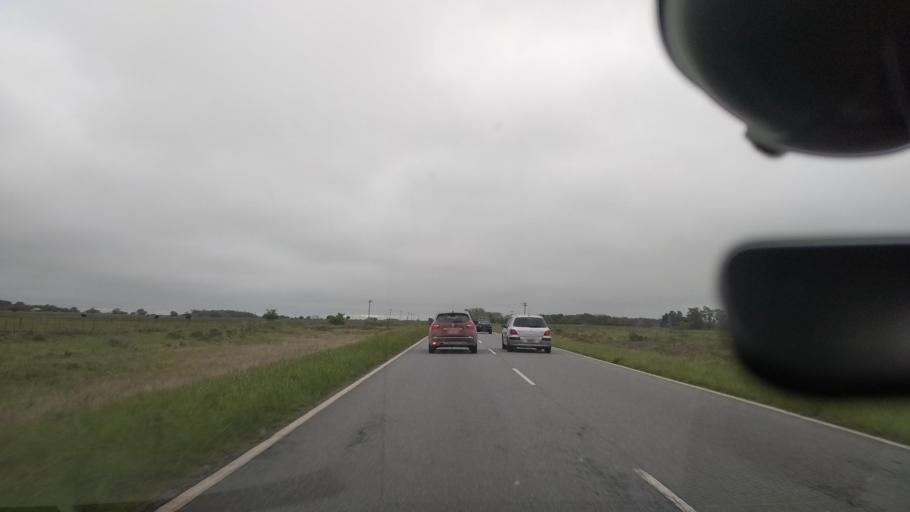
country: AR
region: Buenos Aires
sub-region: Partido de Magdalena
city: Magdalena
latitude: -35.2449
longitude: -57.6778
